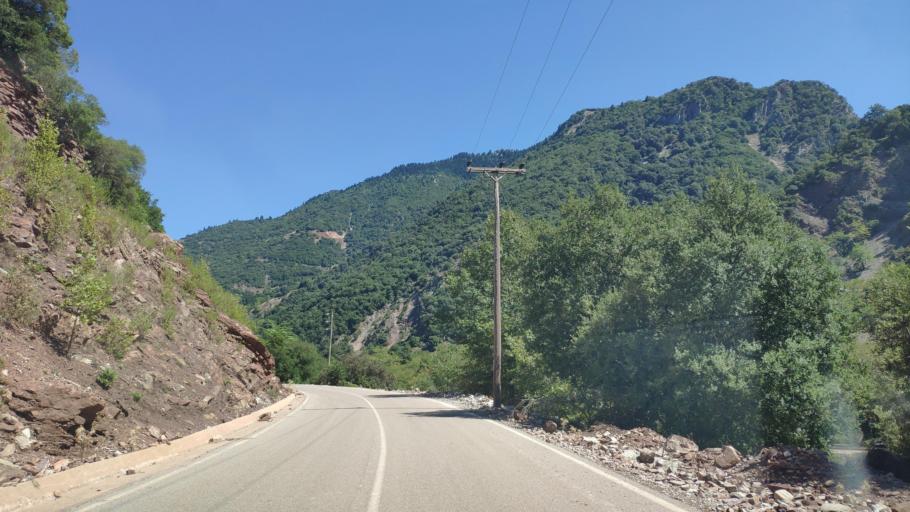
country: GR
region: Central Greece
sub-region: Nomos Evrytanias
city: Kerasochori
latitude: 39.0583
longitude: 21.6069
